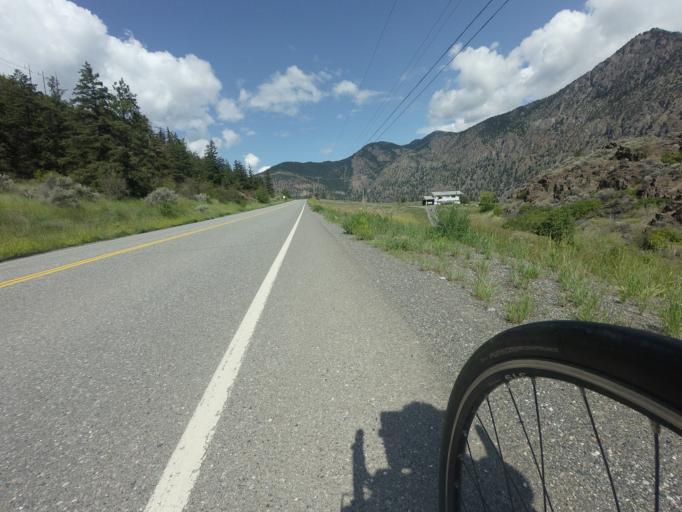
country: CA
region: British Columbia
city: Lillooet
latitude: 50.7567
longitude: -121.8984
